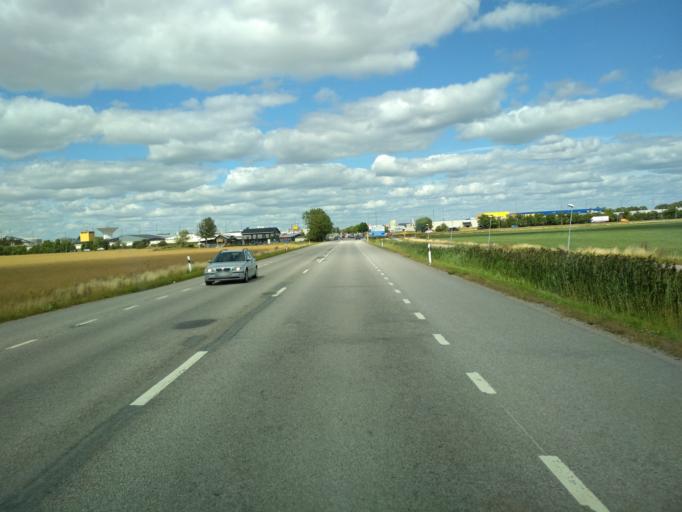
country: SE
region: Uppsala
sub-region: Uppsala Kommun
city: Saevja
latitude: 59.8403
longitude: 17.6895
